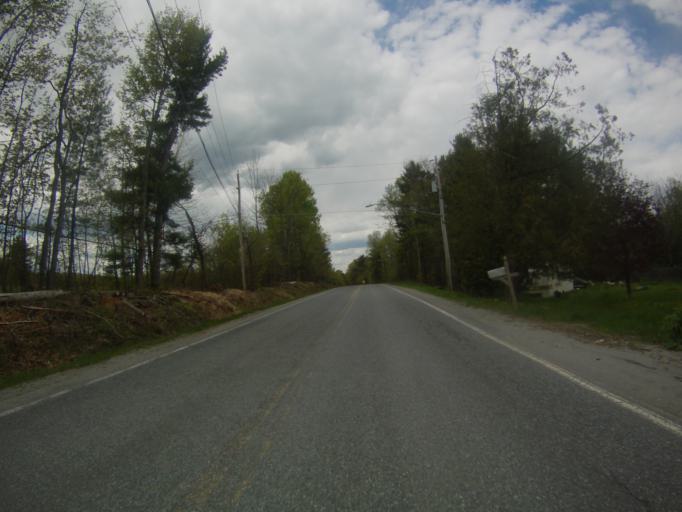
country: US
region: New York
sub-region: Essex County
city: Port Henry
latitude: 44.0061
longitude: -73.4983
